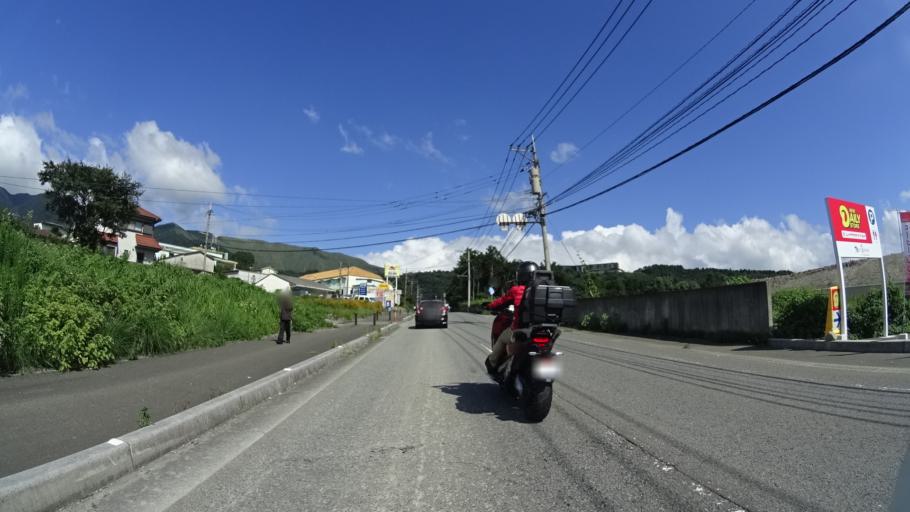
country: JP
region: Oita
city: Beppu
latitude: 33.3106
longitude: 131.4613
